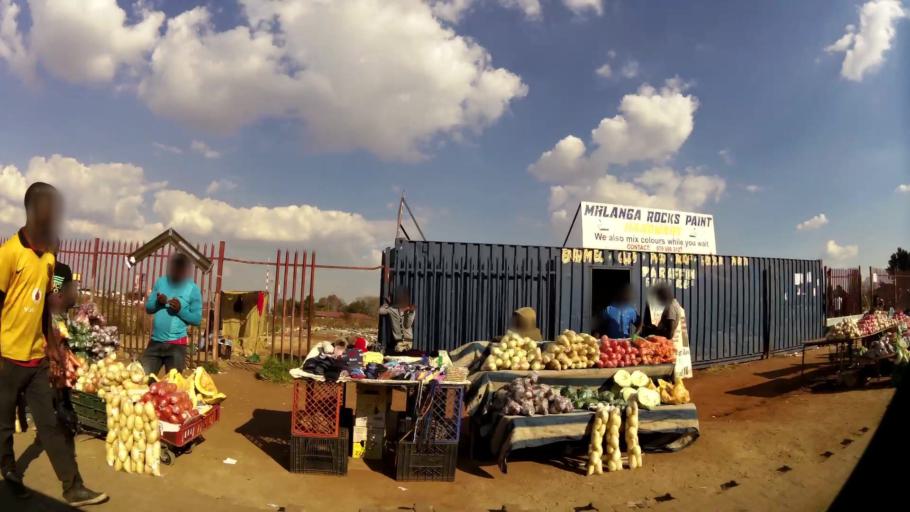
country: ZA
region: Gauteng
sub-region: City of Johannesburg Metropolitan Municipality
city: Roodepoort
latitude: -26.2134
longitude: 27.8693
